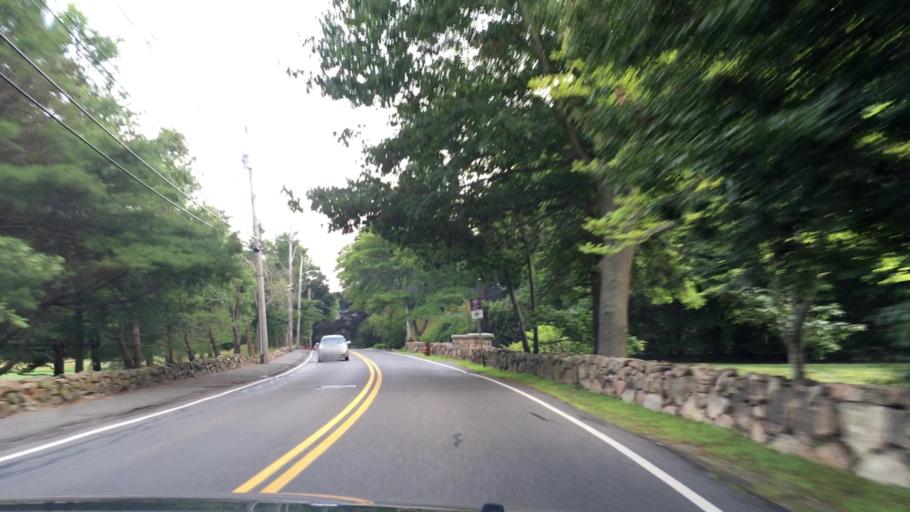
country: US
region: Massachusetts
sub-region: Essex County
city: Essex
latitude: 42.5859
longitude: -70.7685
